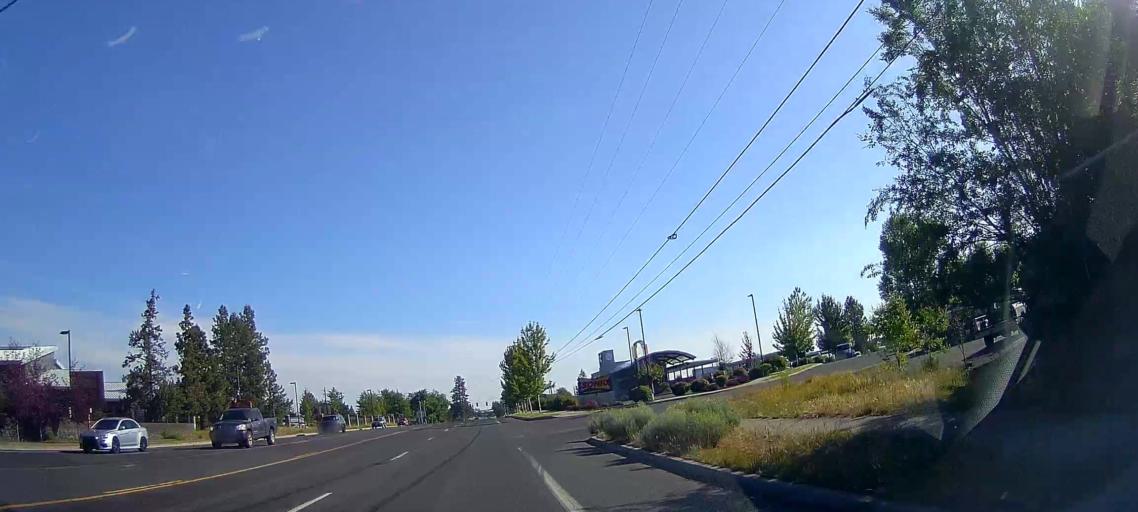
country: US
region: Oregon
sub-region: Deschutes County
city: Bend
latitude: 44.0891
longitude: -121.3057
